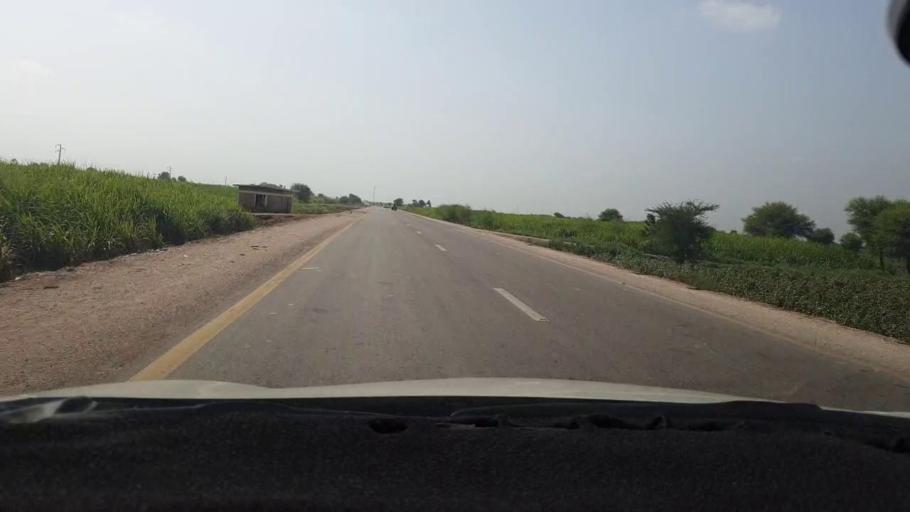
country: PK
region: Sindh
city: Jhol
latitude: 25.8475
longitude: 69.0611
